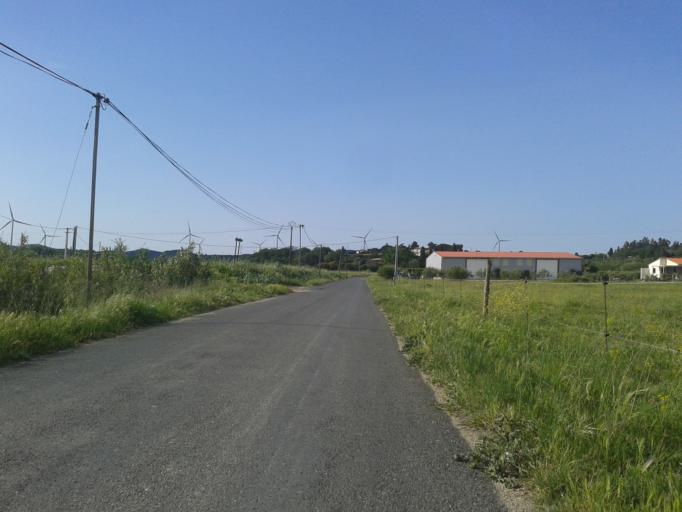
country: FR
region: Languedoc-Roussillon
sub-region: Departement des Pyrenees-Orientales
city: Pezilla-la-Riviere
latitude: 42.6993
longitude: 2.7638
